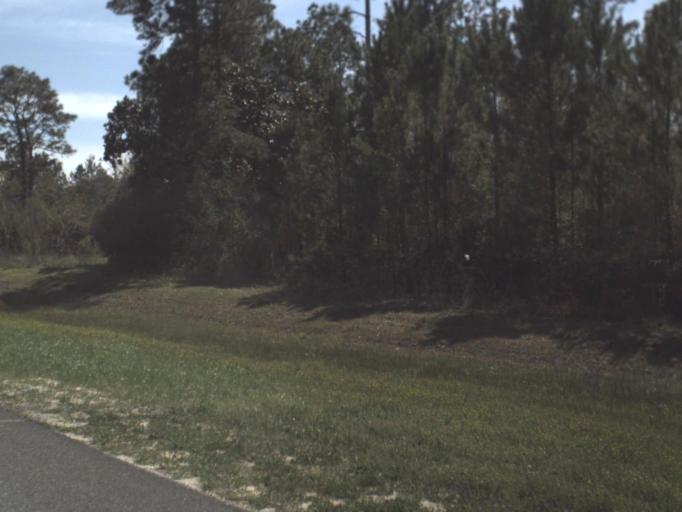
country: US
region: Florida
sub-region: Bay County
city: Lynn Haven
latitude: 30.3668
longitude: -85.6733
